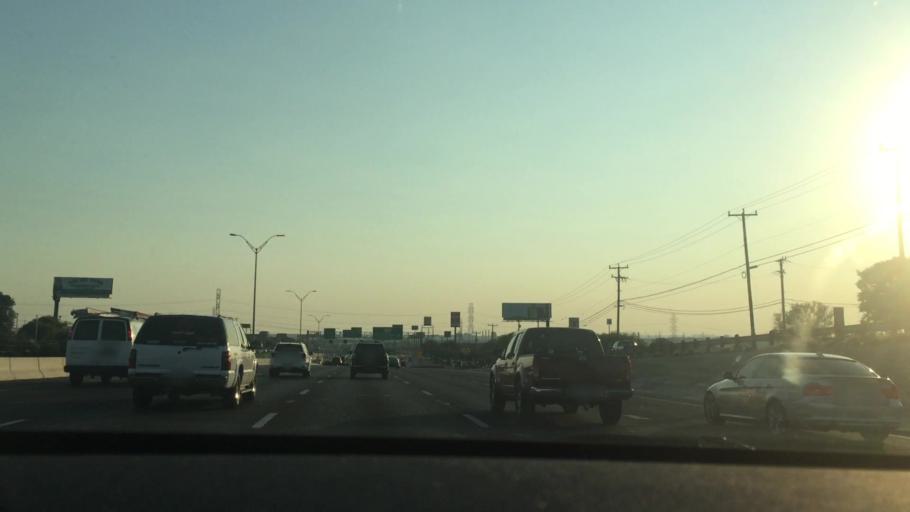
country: US
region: Texas
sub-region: Bexar County
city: Live Oak
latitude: 29.5486
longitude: -98.3640
